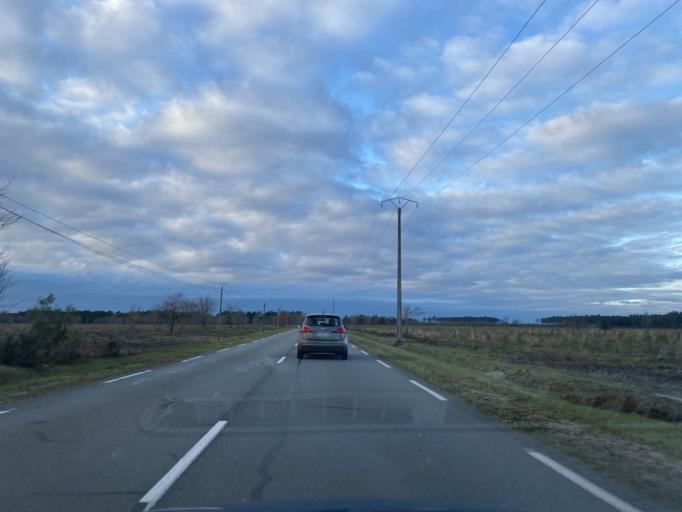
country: FR
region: Aquitaine
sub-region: Departement de la Gironde
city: Marcheprime
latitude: 44.7479
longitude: -0.9115
